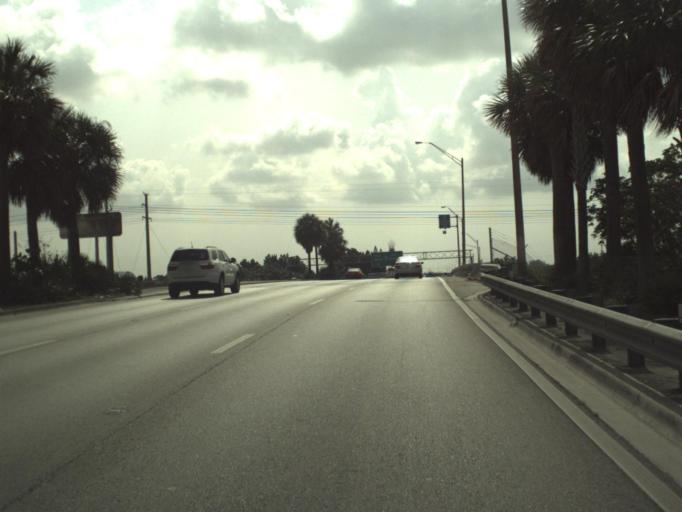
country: US
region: Florida
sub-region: Broward County
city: Lauderhill
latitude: 26.1358
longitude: -80.2198
